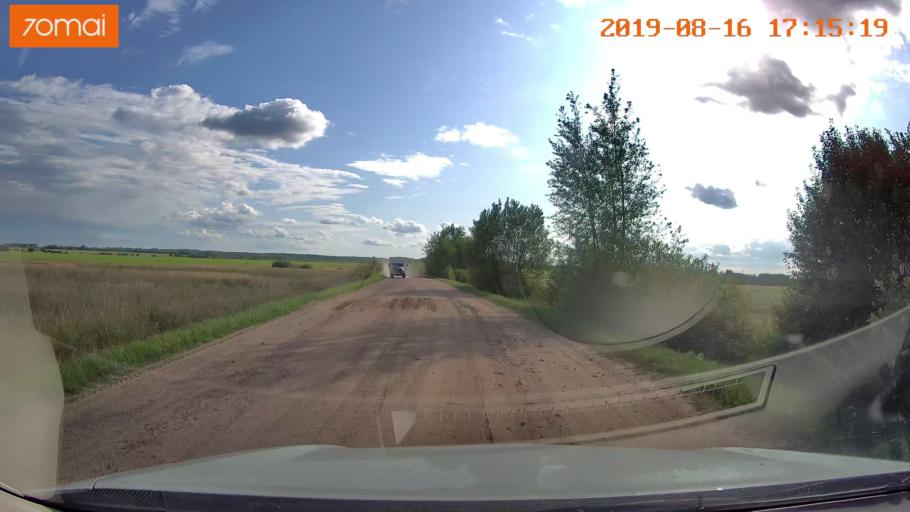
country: BY
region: Mogilev
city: Hlusha
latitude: 53.1796
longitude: 28.8448
